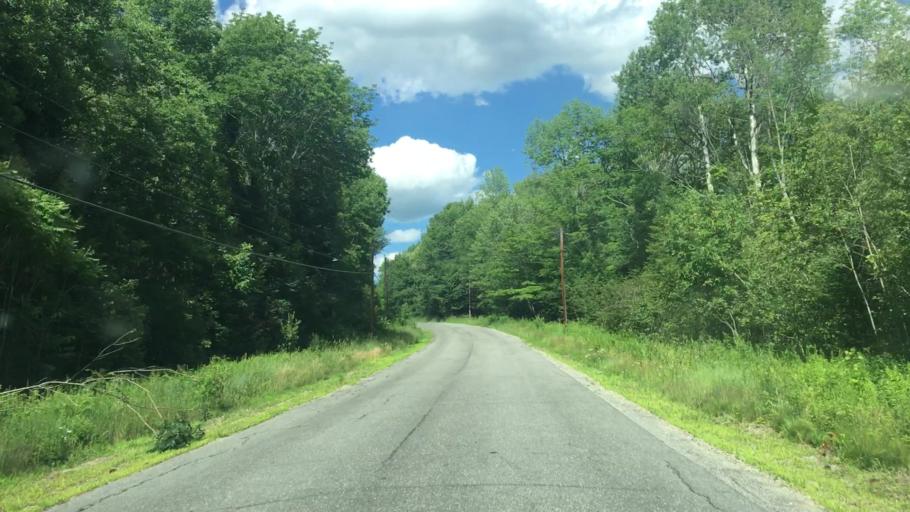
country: US
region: Maine
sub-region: Franklin County
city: Farmington
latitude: 44.6688
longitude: -70.1279
